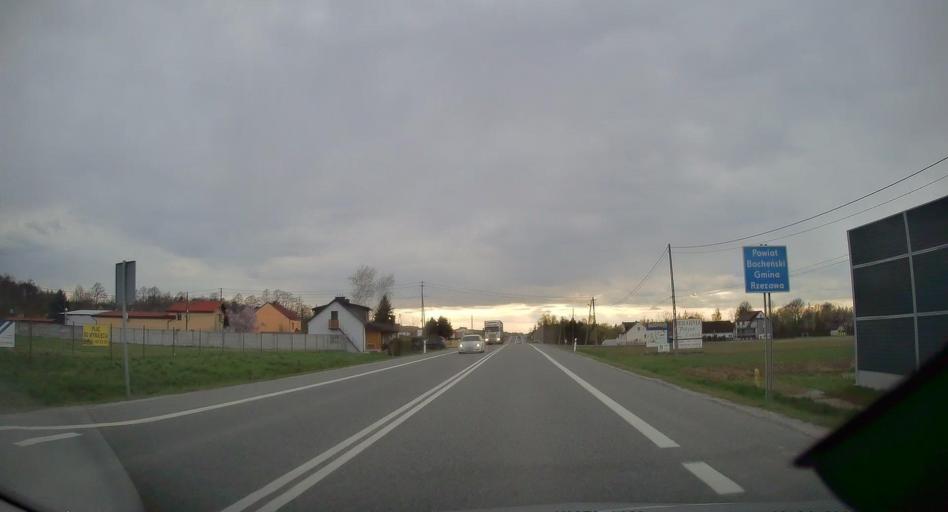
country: PL
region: Lesser Poland Voivodeship
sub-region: Powiat bochenski
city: Jodlowka
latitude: 49.9743
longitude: 20.5519
